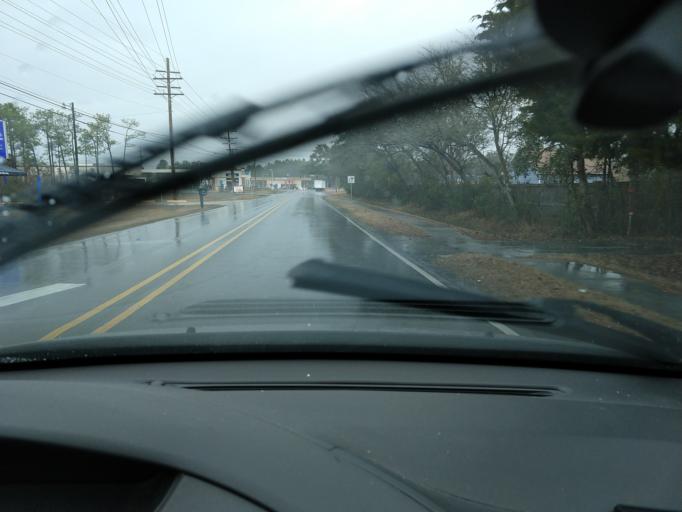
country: US
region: Mississippi
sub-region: Jackson County
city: Gulf Park Estates
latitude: 30.4067
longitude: -88.7576
